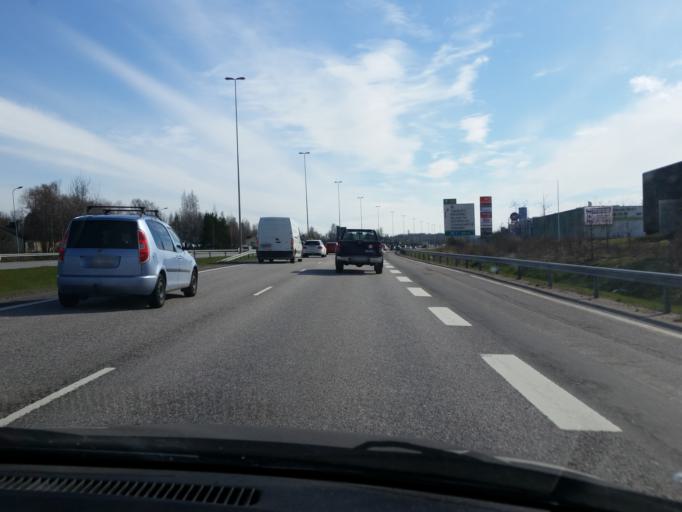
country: FI
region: Uusimaa
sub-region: Helsinki
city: Vantaa
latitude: 60.2780
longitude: 24.9771
